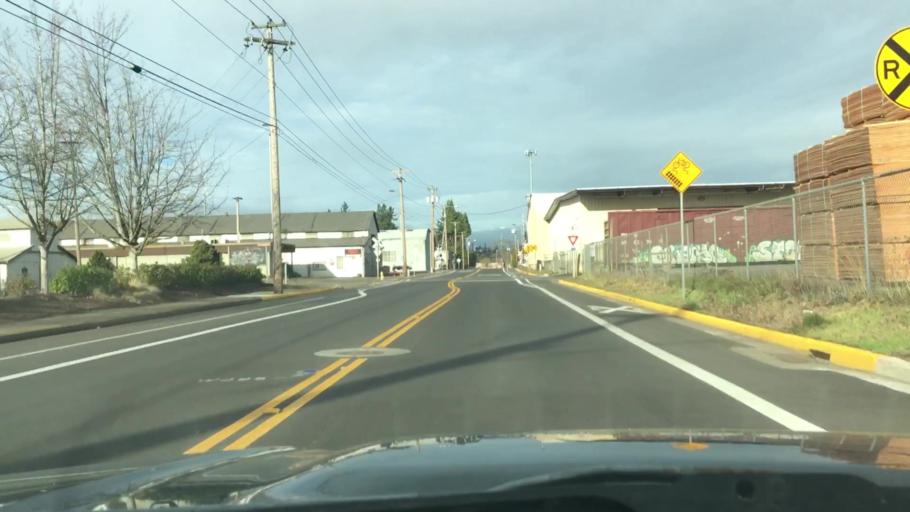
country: US
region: Oregon
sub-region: Lane County
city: Eugene
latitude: 44.0588
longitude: -123.1227
